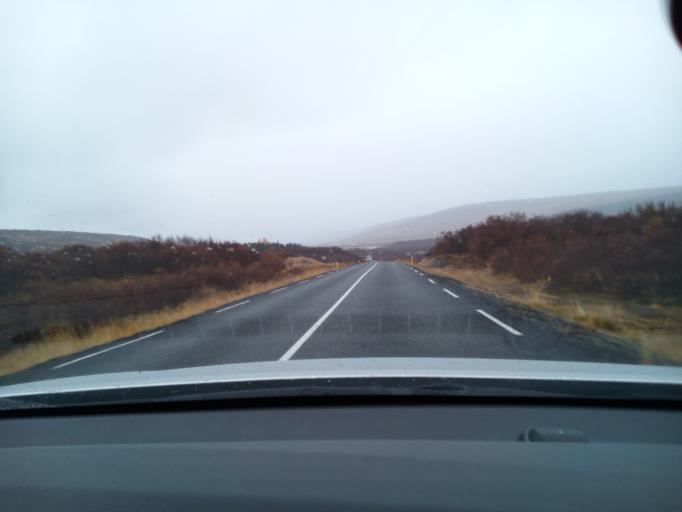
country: IS
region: South
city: Hveragerdi
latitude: 64.7015
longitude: -20.9848
